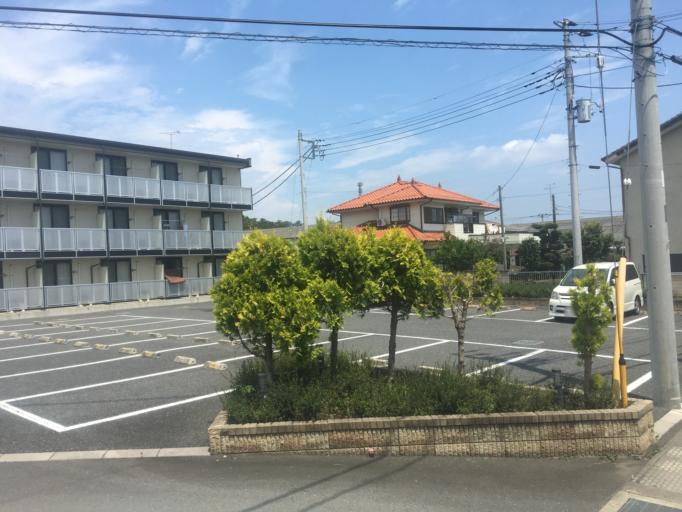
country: JP
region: Saitama
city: Kodamacho-kodamaminami
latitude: 36.1904
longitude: 139.1380
